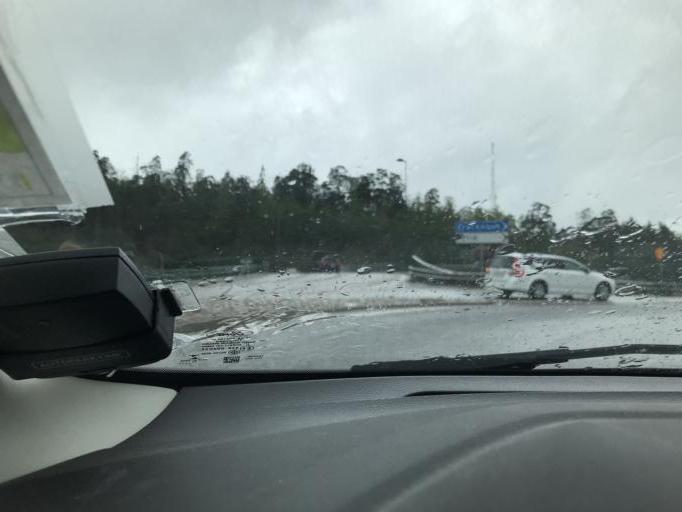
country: SE
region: Stockholm
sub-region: Botkyrka Kommun
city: Alby
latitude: 59.2398
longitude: 17.8367
